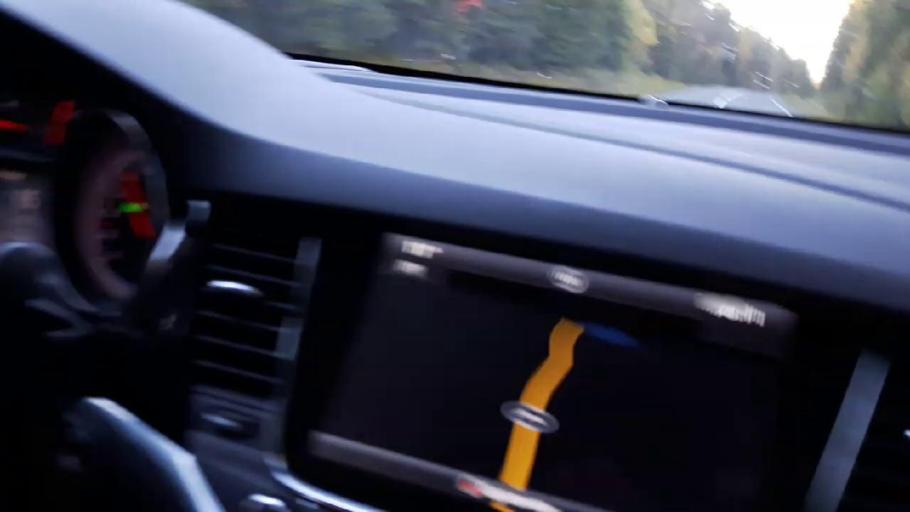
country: SE
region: Jaemtland
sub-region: OEstersunds Kommun
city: Lit
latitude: 63.3637
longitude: 14.8424
